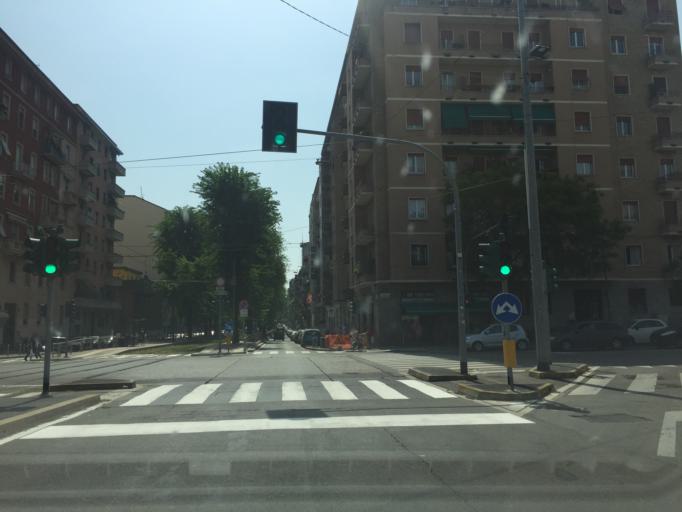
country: IT
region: Lombardy
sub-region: Citta metropolitana di Milano
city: Milano
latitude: 45.4914
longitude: 9.1611
